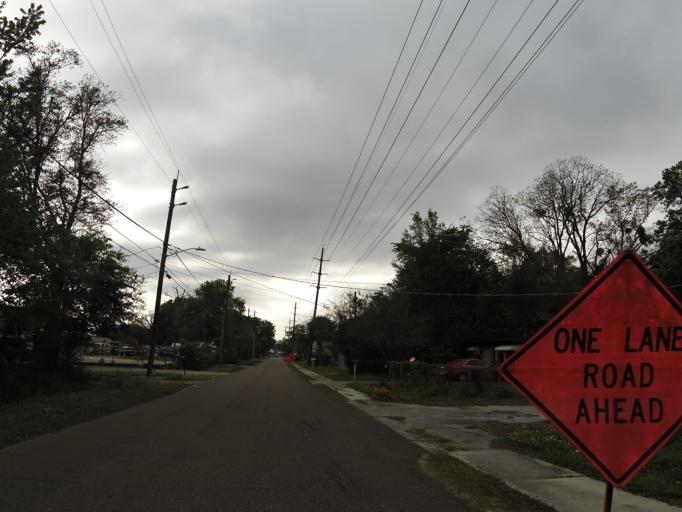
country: US
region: Florida
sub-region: Duval County
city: Jacksonville
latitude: 30.3225
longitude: -81.7244
